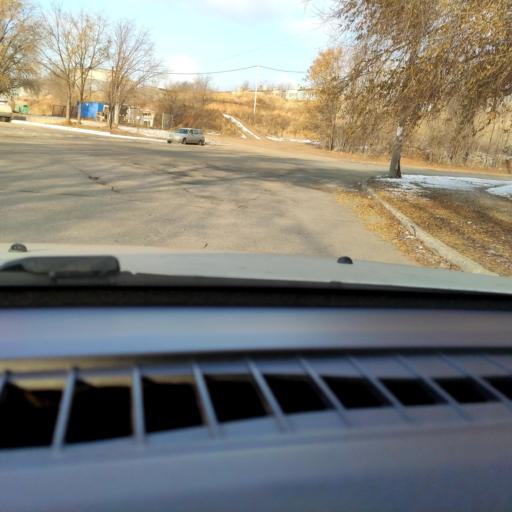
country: RU
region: Samara
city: Tol'yatti
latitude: 53.5023
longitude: 49.2508
